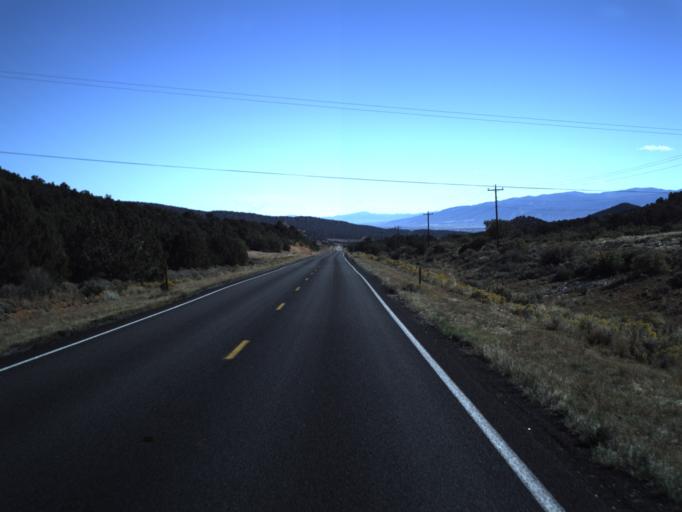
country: US
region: Utah
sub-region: Iron County
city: Cedar City
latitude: 37.6165
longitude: -113.3348
